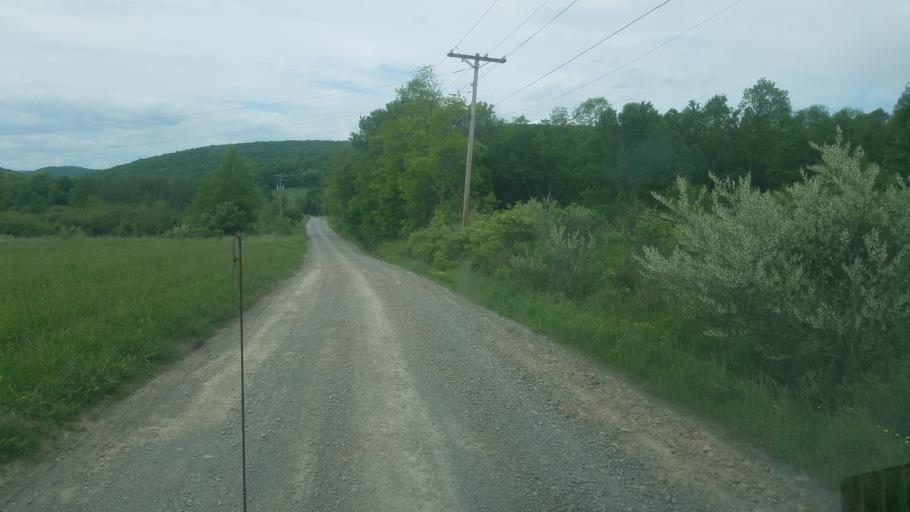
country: US
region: Pennsylvania
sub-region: Tioga County
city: Westfield
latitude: 41.8787
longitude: -77.5961
